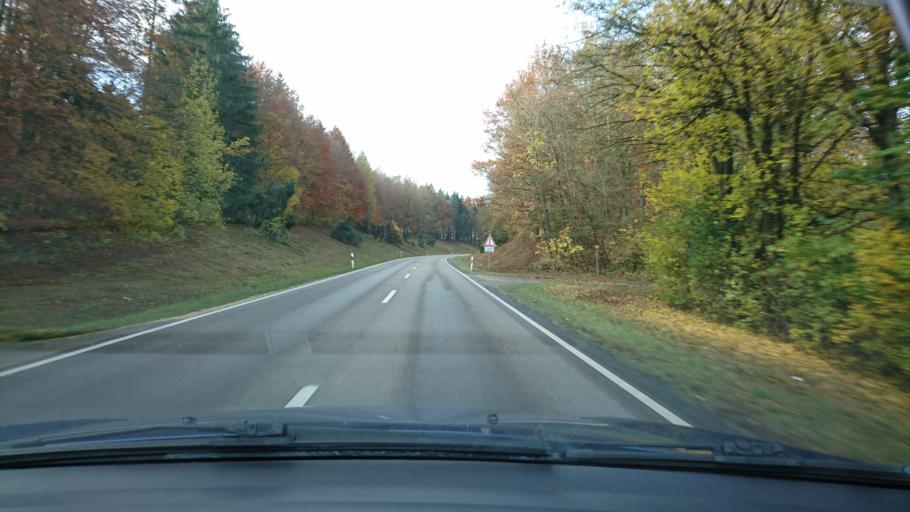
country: DE
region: Bavaria
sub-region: Swabia
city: Bissingen
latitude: 48.7218
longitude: 10.5936
